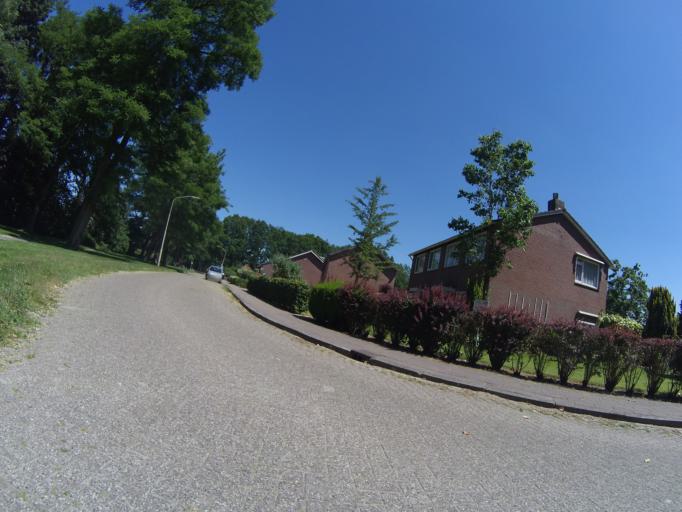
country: NL
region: Drenthe
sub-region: Gemeente Emmen
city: Emmen
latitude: 52.8000
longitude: 6.9298
